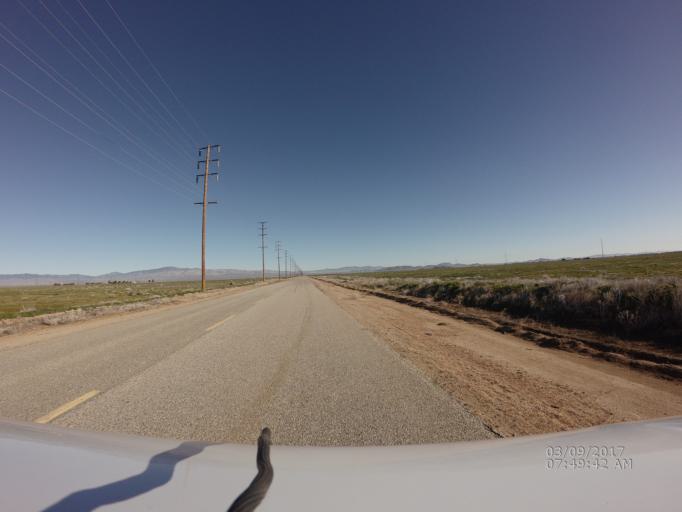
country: US
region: California
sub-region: Los Angeles County
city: Leona Valley
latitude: 34.7618
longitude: -118.3254
